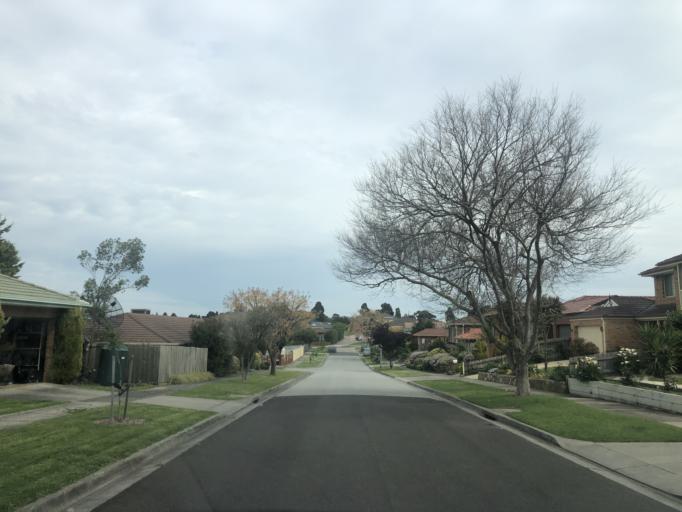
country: AU
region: Victoria
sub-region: Casey
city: Hallam
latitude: -38.0043
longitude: 145.2773
